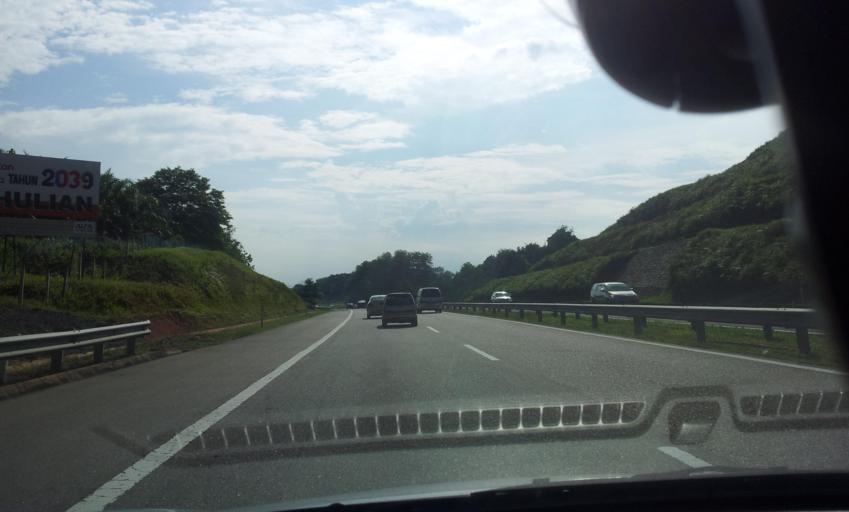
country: MY
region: Pahang
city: Mentekab
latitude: 3.5311
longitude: 102.2064
